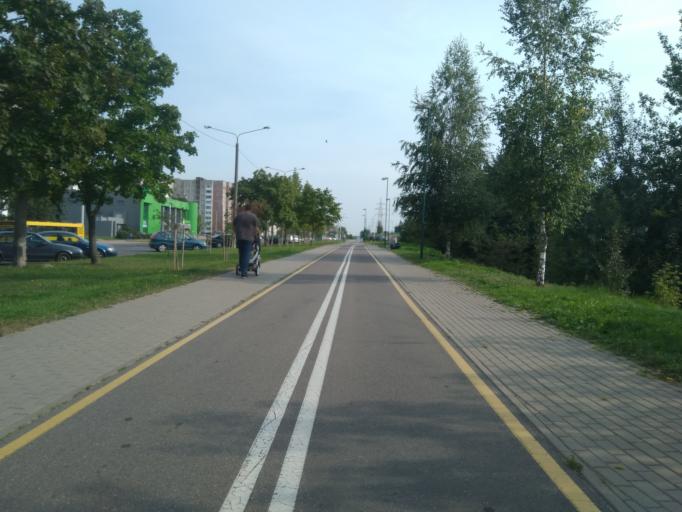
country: BY
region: Minsk
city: Minsk
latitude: 53.8630
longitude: 27.5865
